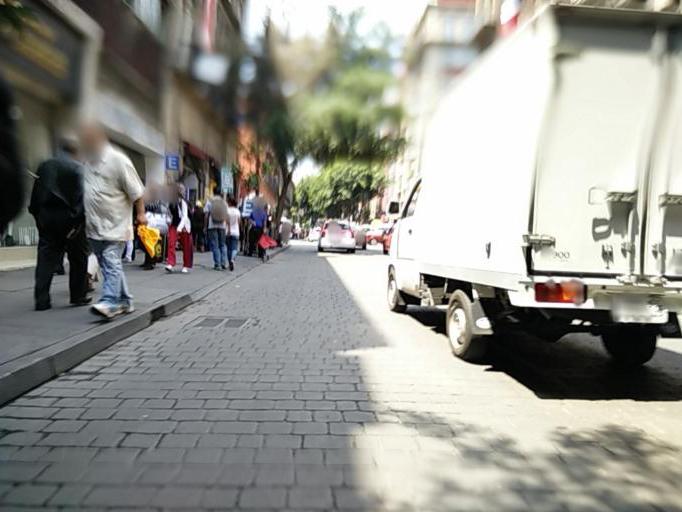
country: MX
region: Mexico City
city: Mexico City
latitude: 19.4352
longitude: -99.1345
